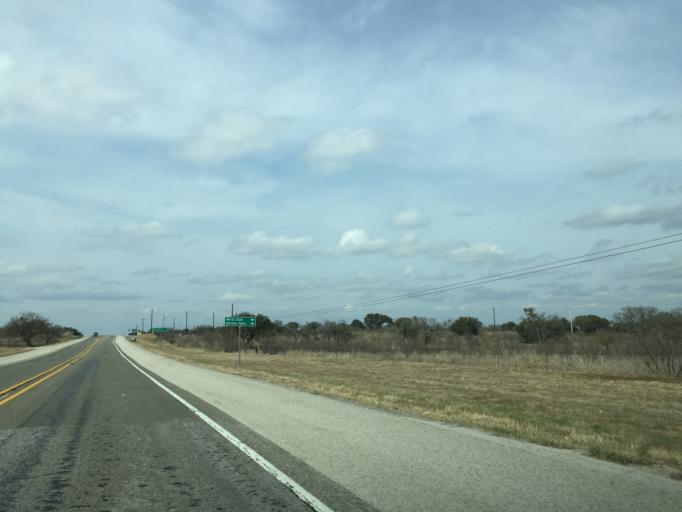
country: US
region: Texas
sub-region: Burnet County
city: Granite Shoals
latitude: 30.5179
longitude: -98.4062
